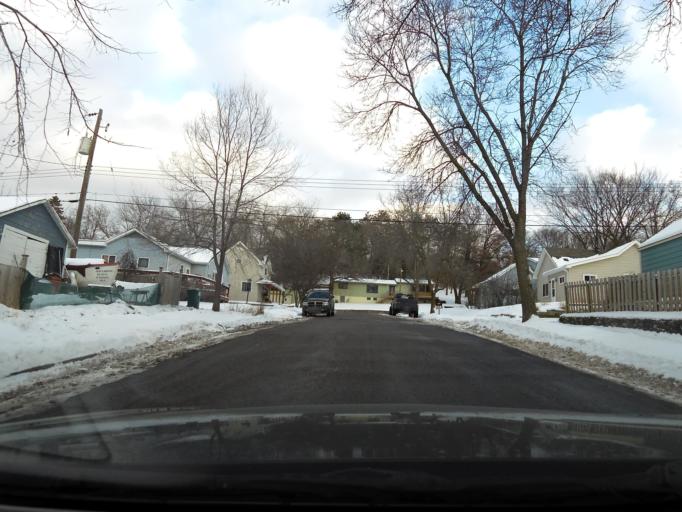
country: US
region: Wisconsin
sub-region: Saint Croix County
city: Hudson
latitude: 44.9787
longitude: -92.7462
